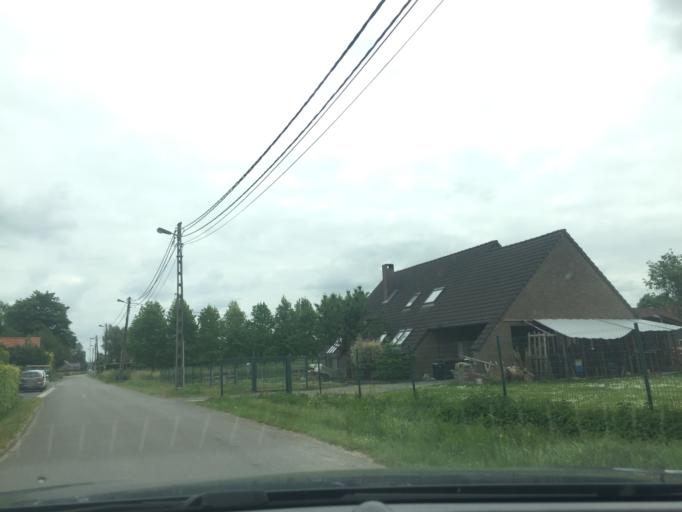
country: BE
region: Wallonia
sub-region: Province du Hainaut
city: Pecq
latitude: 50.6399
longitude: 3.3217
